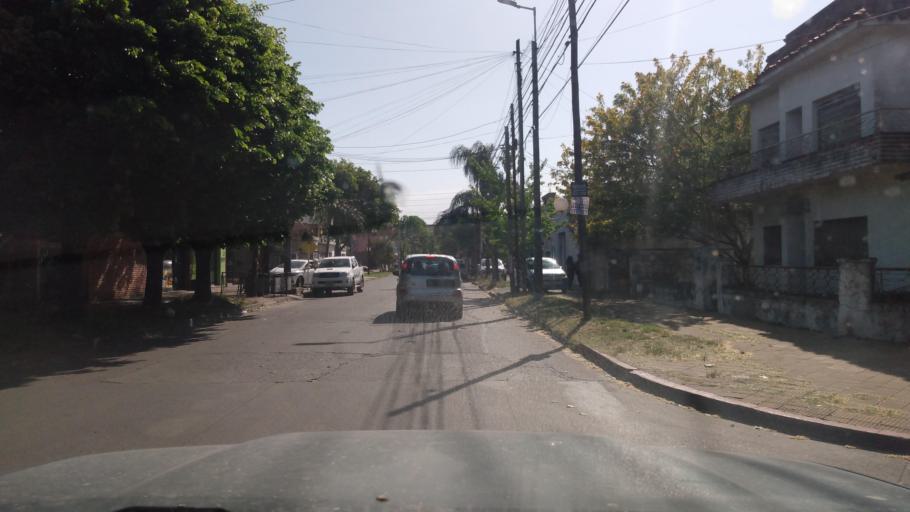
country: AR
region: Buenos Aires
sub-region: Partido de Moron
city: Moron
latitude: -34.6483
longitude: -58.5913
